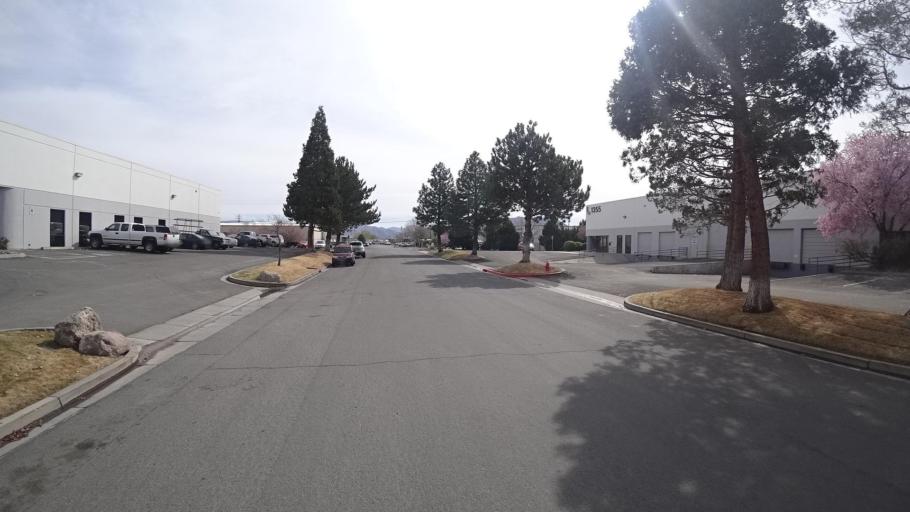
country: US
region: Nevada
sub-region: Washoe County
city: Sparks
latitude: 39.5200
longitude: -119.7605
